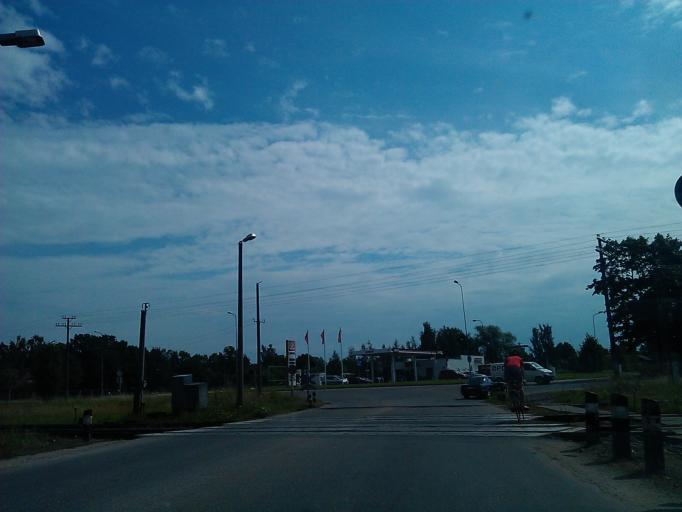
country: LV
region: Cesu Rajons
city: Cesis
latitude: 57.3201
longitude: 25.2898
